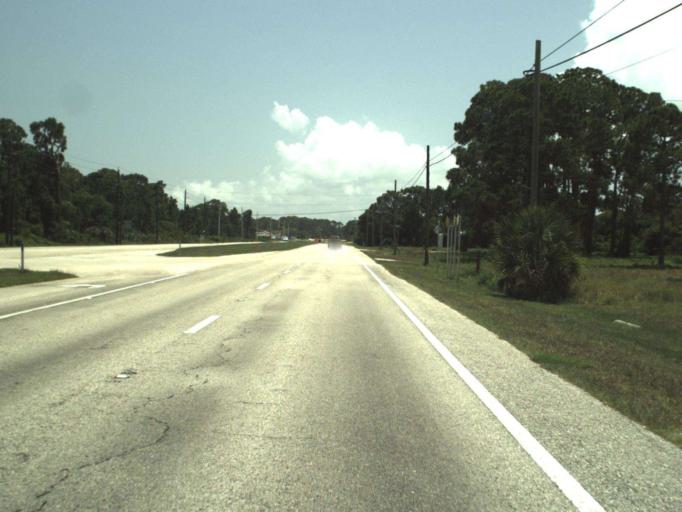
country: US
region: Florida
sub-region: Volusia County
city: Oak Hill
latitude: 28.8827
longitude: -80.8559
